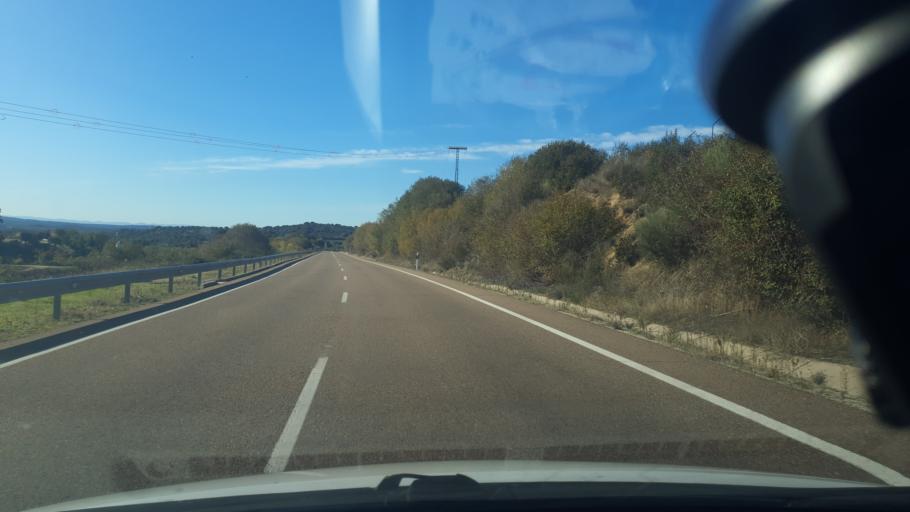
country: ES
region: Castille and Leon
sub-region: Provincia de Avila
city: Poyales del Hoyo
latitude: 40.1631
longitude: -5.1435
